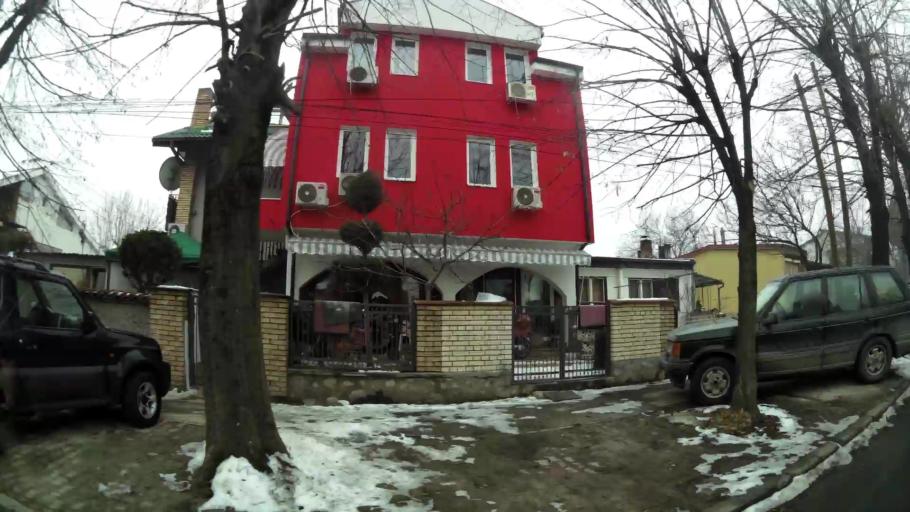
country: MK
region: Cair
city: Cair
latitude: 42.0156
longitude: 21.4601
